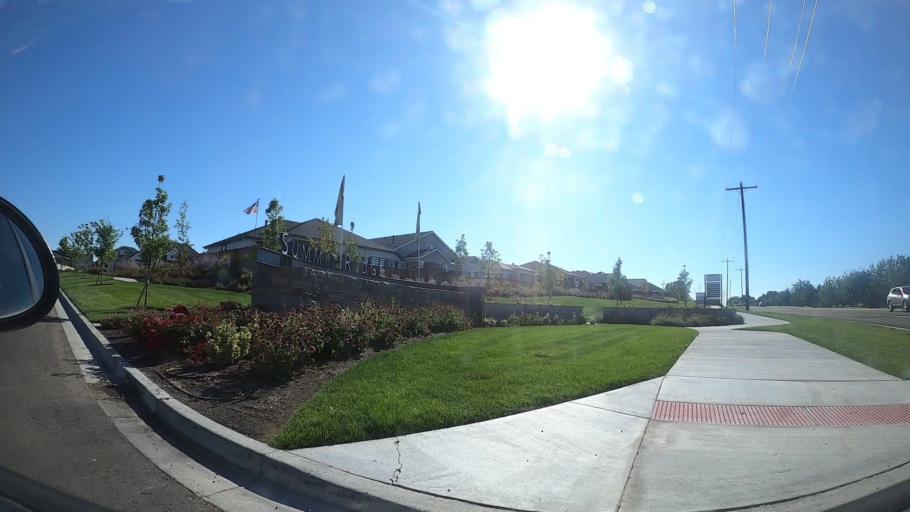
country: US
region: Idaho
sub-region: Canyon County
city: Nampa
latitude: 43.5473
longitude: -116.6003
